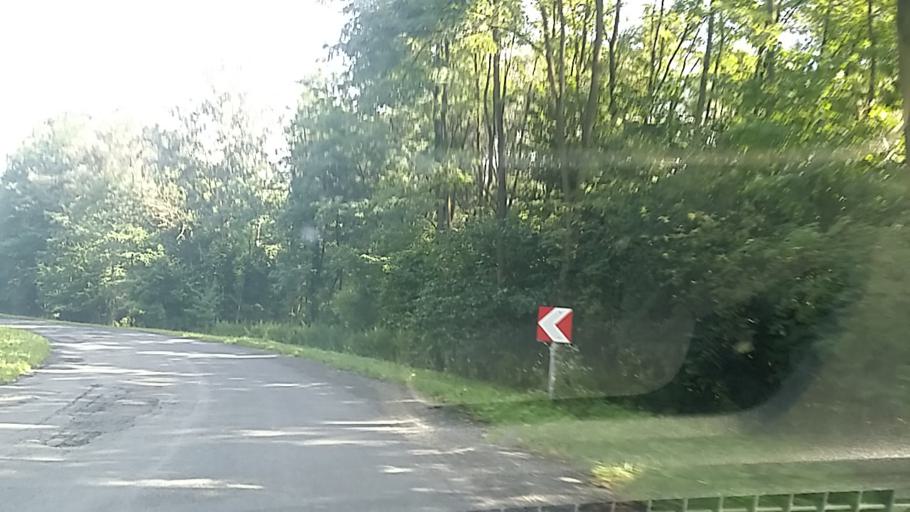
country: HU
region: Zala
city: Letenye
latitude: 46.5297
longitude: 16.7114
